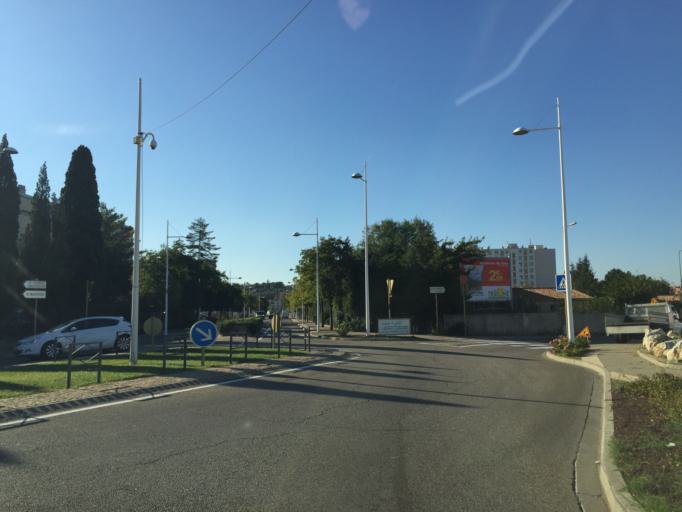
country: FR
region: Provence-Alpes-Cote d'Azur
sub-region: Departement du Vaucluse
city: Bollene
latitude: 44.2867
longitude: 4.7508
